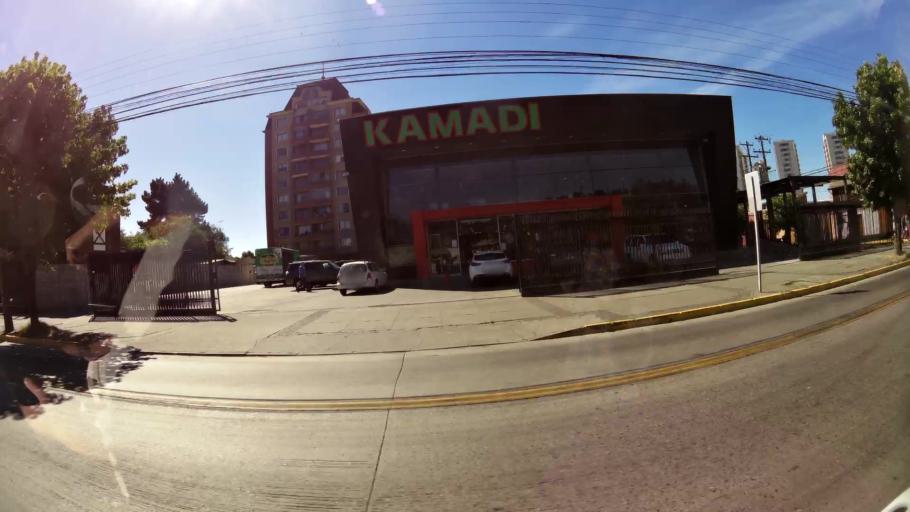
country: CL
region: Biobio
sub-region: Provincia de Concepcion
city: Concepcion
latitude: -36.8160
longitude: -73.0346
